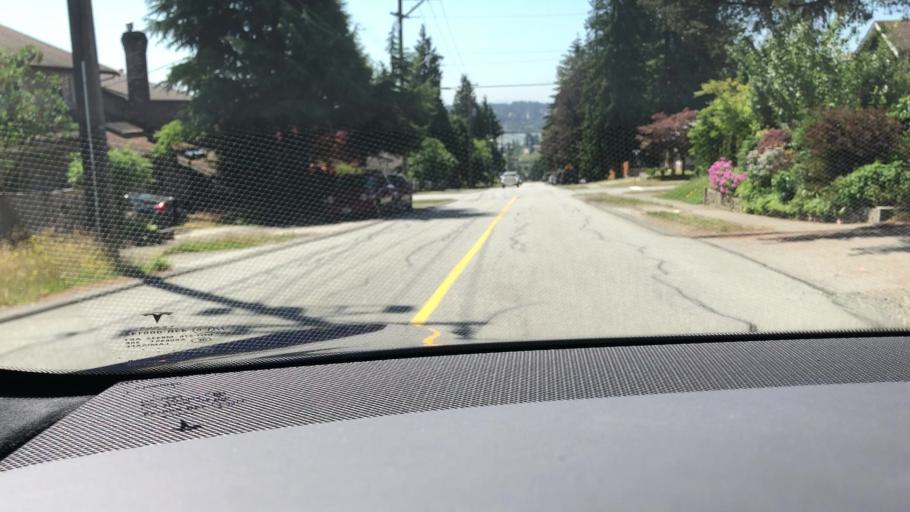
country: CA
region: British Columbia
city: Port Moody
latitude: 49.2469
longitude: -122.8652
